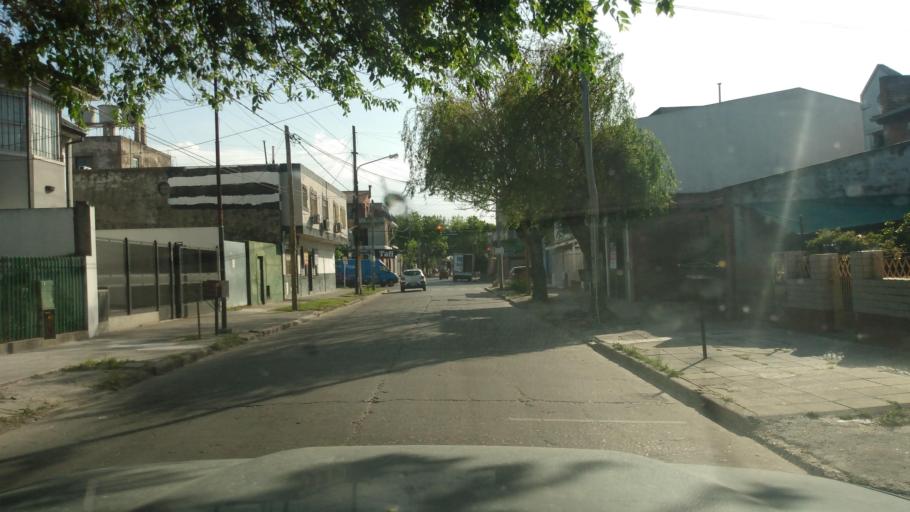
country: AR
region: Buenos Aires
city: San Justo
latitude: -34.6782
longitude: -58.5688
